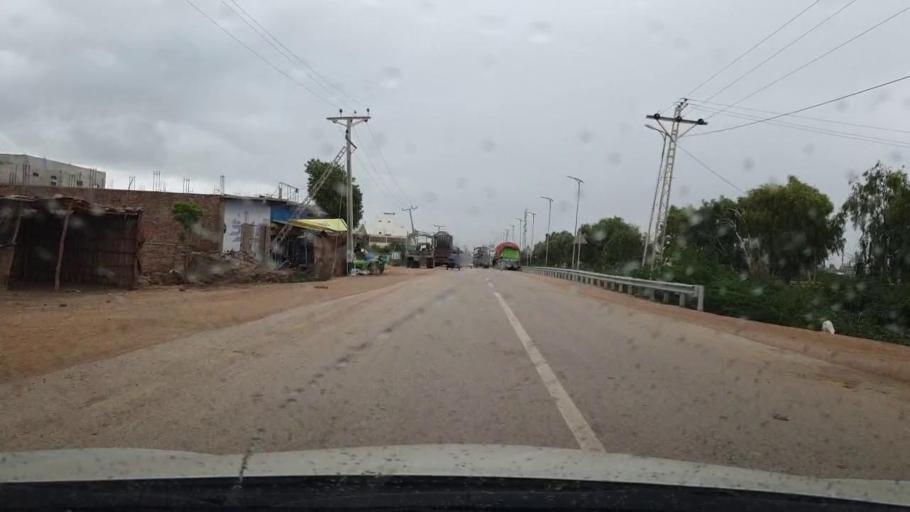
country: PK
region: Sindh
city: Kario
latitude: 24.6532
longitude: 68.5253
